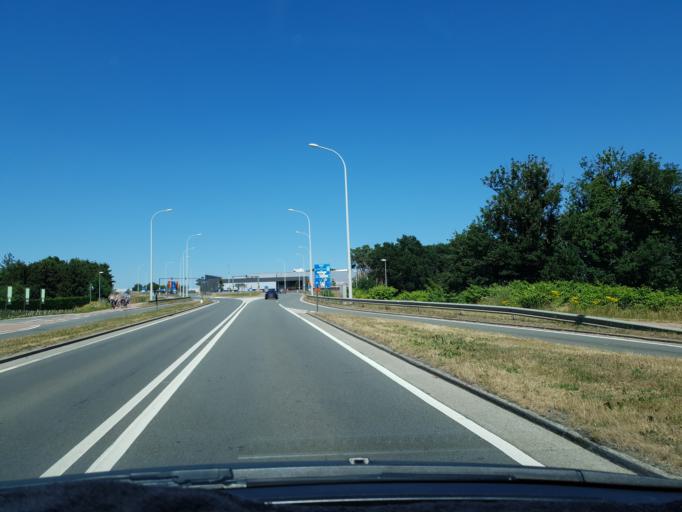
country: BE
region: Flanders
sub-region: Provincie Antwerpen
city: Herentals
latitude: 51.1673
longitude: 4.8474
